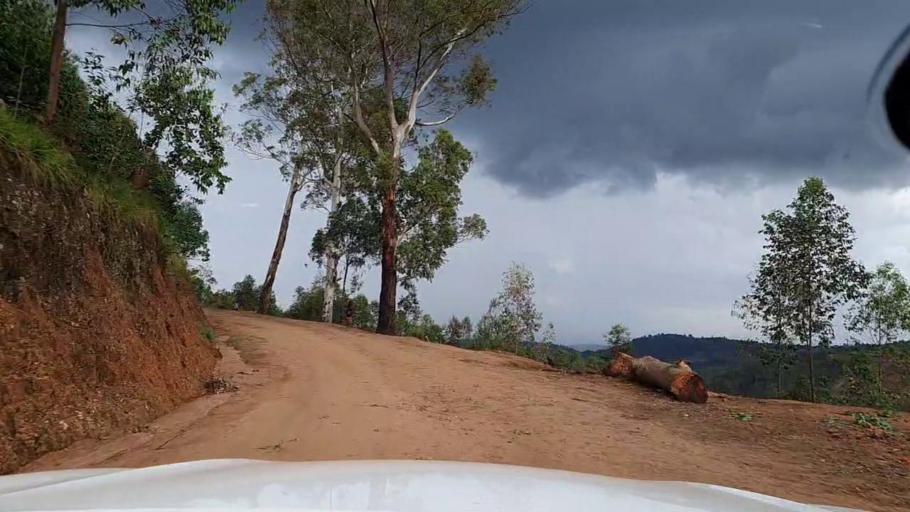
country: BI
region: Kayanza
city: Kayanza
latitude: -2.7909
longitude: 29.5250
